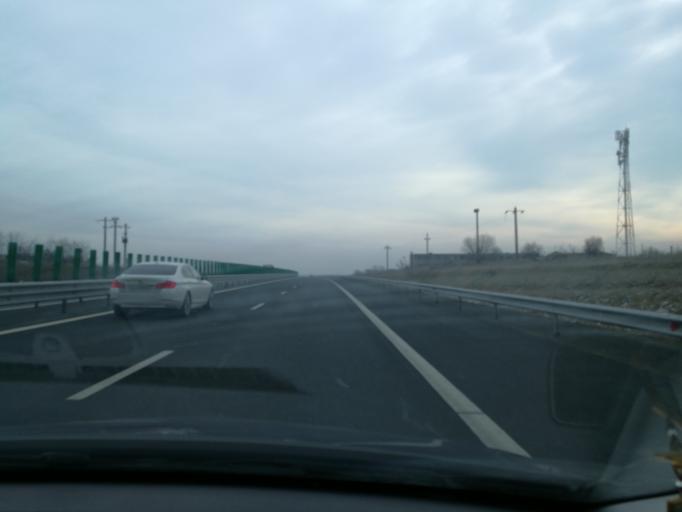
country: RO
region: Constanta
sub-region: Comuna Mircea Voda
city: Satu Nou
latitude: 44.2179
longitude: 28.1997
